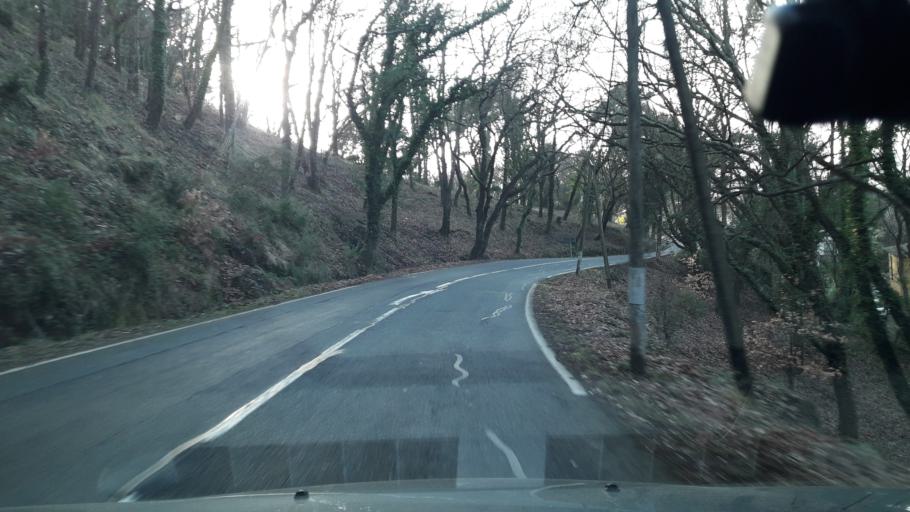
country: FR
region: Provence-Alpes-Cote d'Azur
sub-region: Departement du Var
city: Tanneron
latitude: 43.5184
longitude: 6.8394
